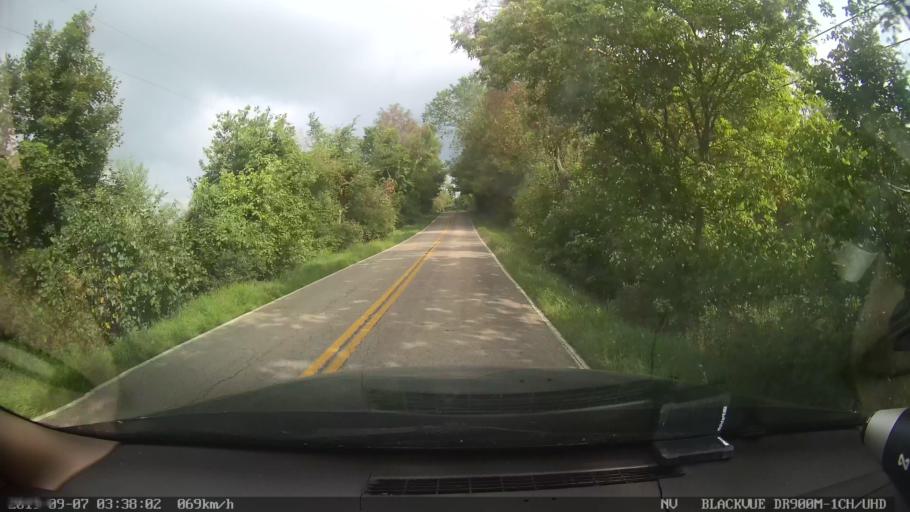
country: US
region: Ohio
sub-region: Licking County
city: Granville
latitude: 40.1001
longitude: -82.5388
